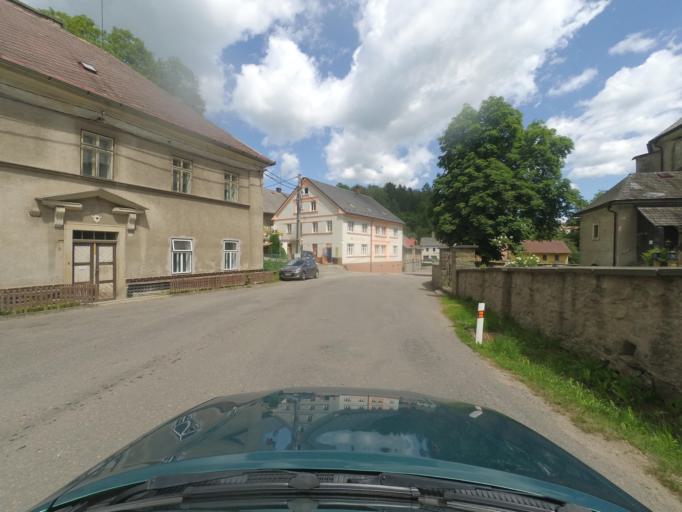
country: CZ
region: Pardubicky
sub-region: Okres Usti nad Orlici
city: Kunvald
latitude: 50.1117
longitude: 16.5531
